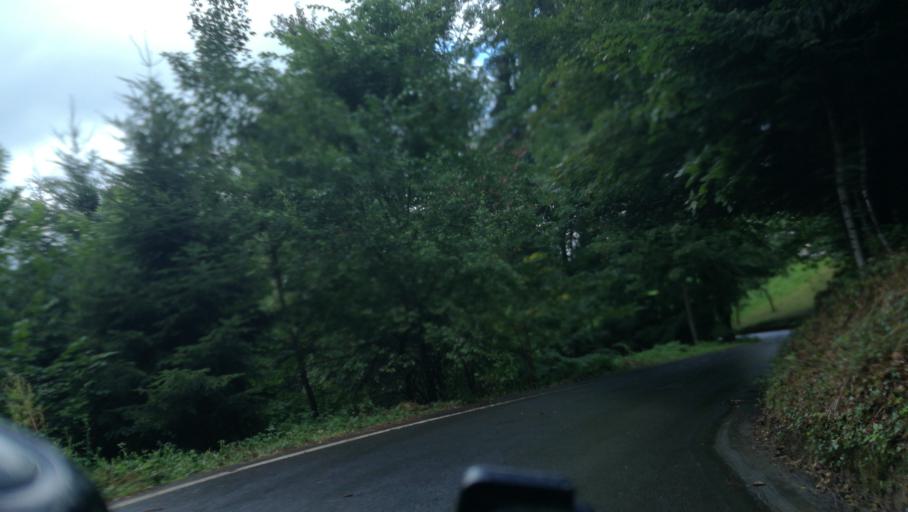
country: CH
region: Zug
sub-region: Zug
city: Zug
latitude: 47.1591
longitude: 8.5298
